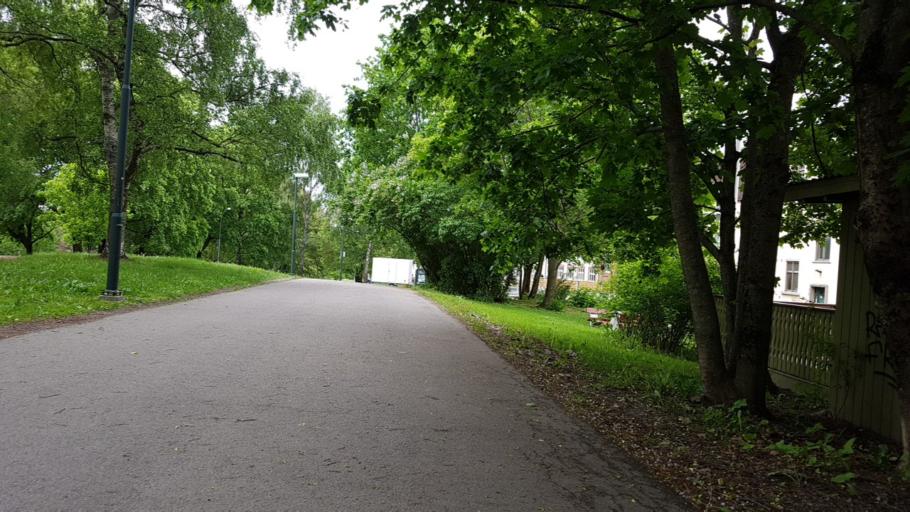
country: NO
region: Oslo
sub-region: Oslo
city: Oslo
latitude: 59.9355
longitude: 10.7772
